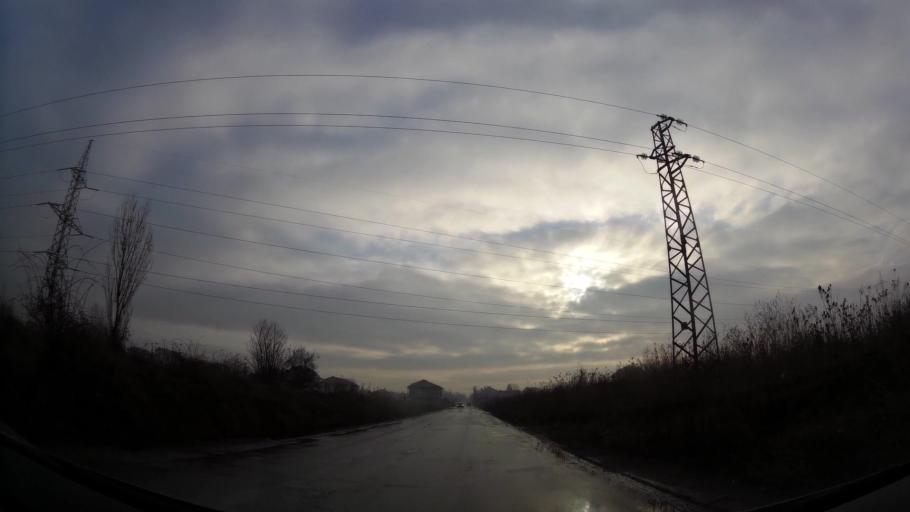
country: BG
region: Sofia-Capital
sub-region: Stolichna Obshtina
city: Sofia
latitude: 42.7385
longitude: 23.3344
